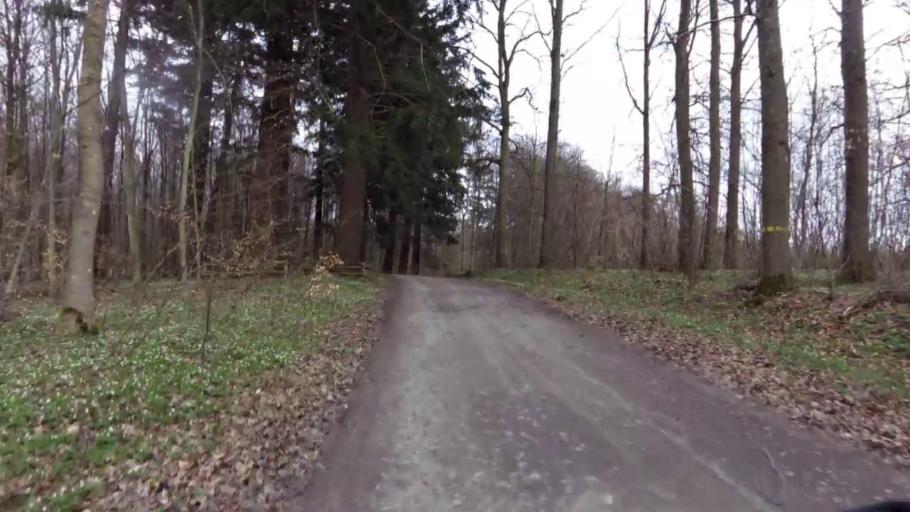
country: PL
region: West Pomeranian Voivodeship
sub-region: Powiat koszalinski
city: Sianow
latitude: 54.2675
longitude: 16.3163
